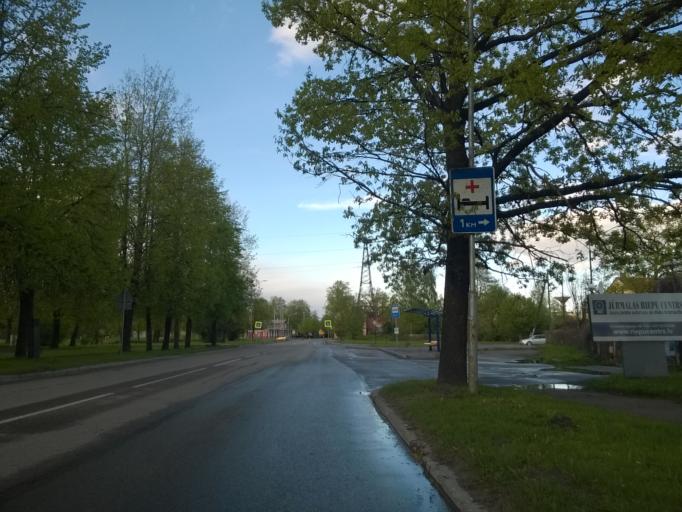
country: LV
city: Tireli
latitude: 56.9457
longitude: 23.6142
